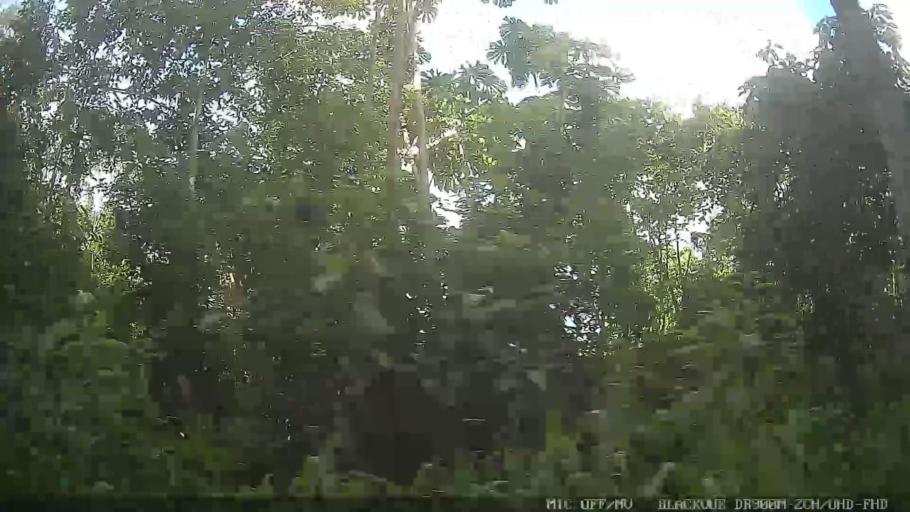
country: BR
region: Minas Gerais
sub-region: Extrema
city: Extrema
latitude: -22.8248
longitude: -46.2521
